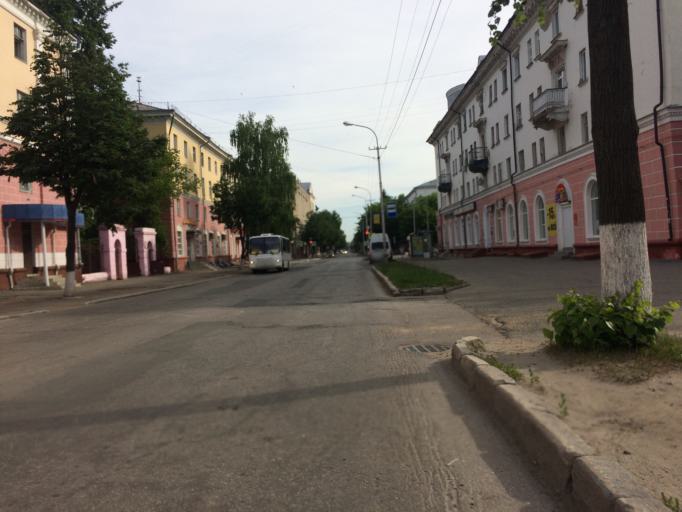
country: RU
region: Mariy-El
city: Yoshkar-Ola
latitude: 56.6288
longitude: 47.8929
